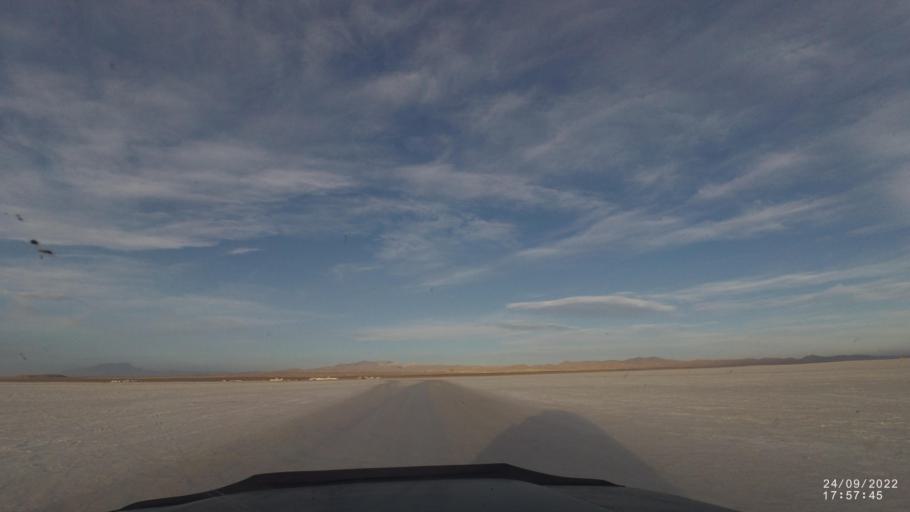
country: BO
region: Potosi
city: Colchani
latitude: -20.3188
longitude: -66.9868
